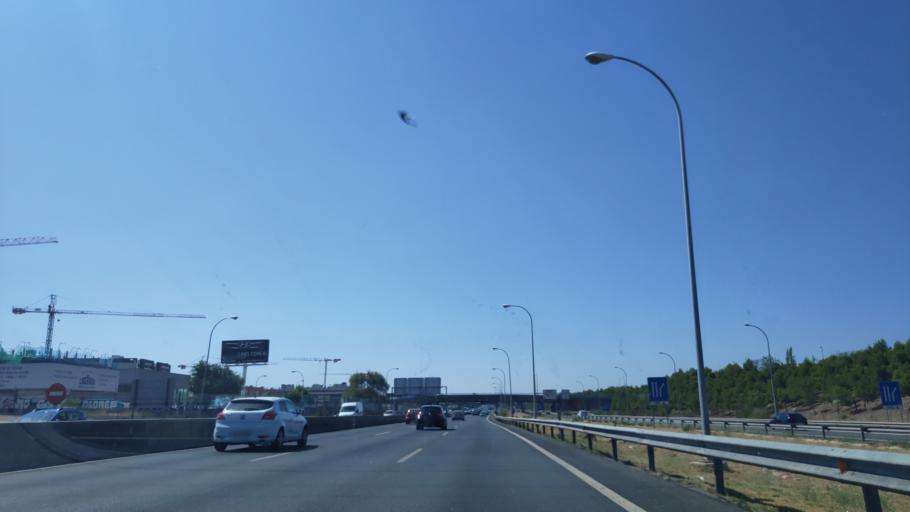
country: ES
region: Madrid
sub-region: Provincia de Madrid
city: Getafe
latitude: 40.3223
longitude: -3.7310
